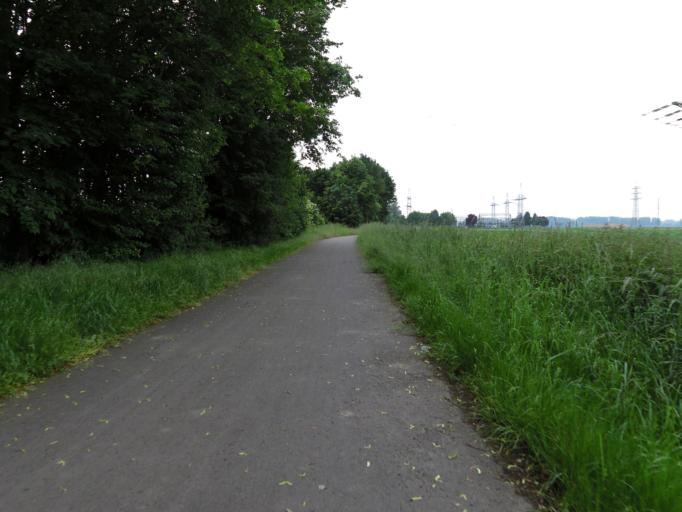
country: DE
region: Hesse
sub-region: Regierungsbezirk Darmstadt
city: Burstadt
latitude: 49.6388
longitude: 8.4228
